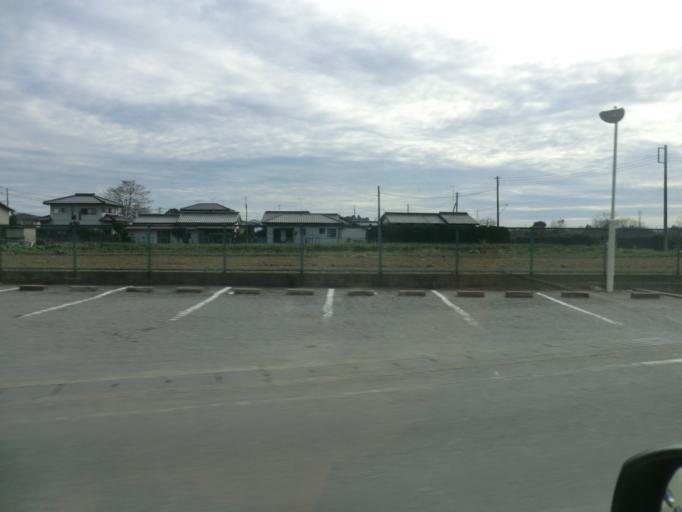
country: JP
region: Ibaraki
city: Mitsukaido
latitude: 36.0451
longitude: 140.0428
